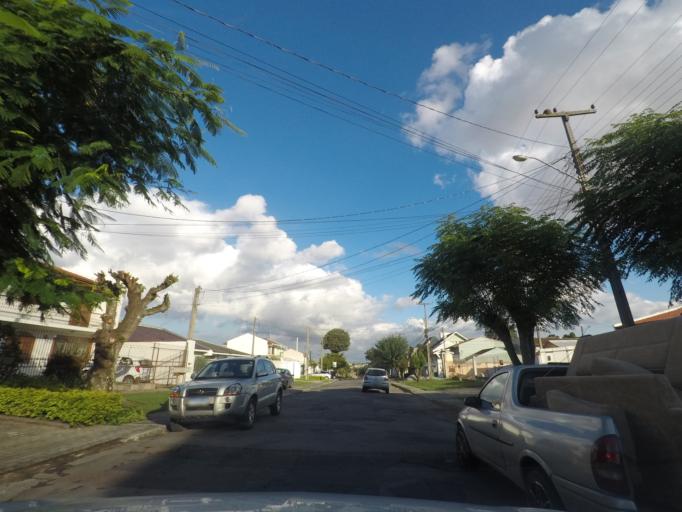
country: BR
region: Parana
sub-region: Curitiba
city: Curitiba
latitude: -25.4866
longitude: -49.2601
